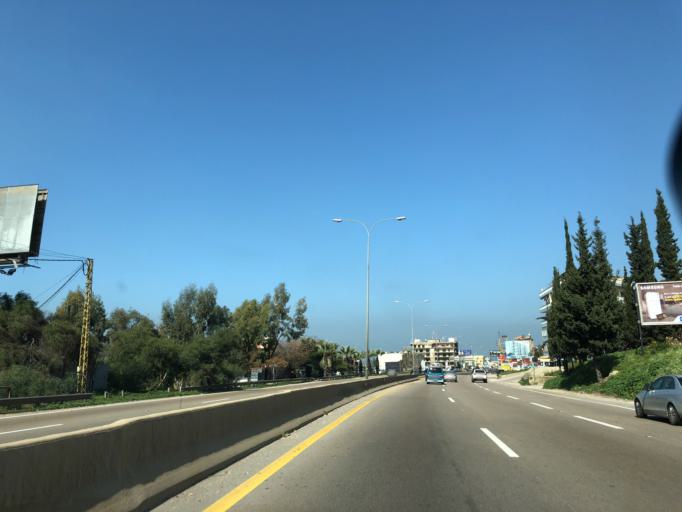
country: LB
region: Mont-Liban
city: Djounie
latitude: 34.0206
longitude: 35.6328
